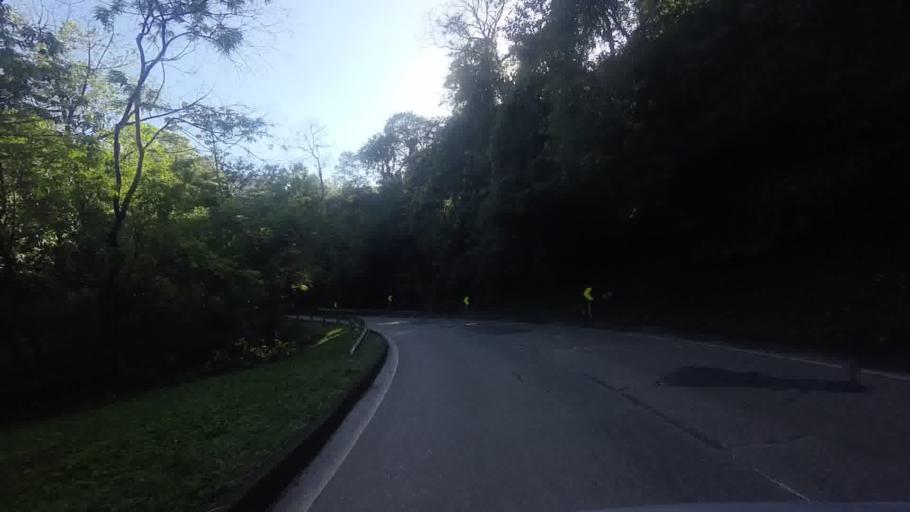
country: BR
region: Rio de Janeiro
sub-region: Petropolis
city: Petropolis
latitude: -22.5606
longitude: -43.2340
